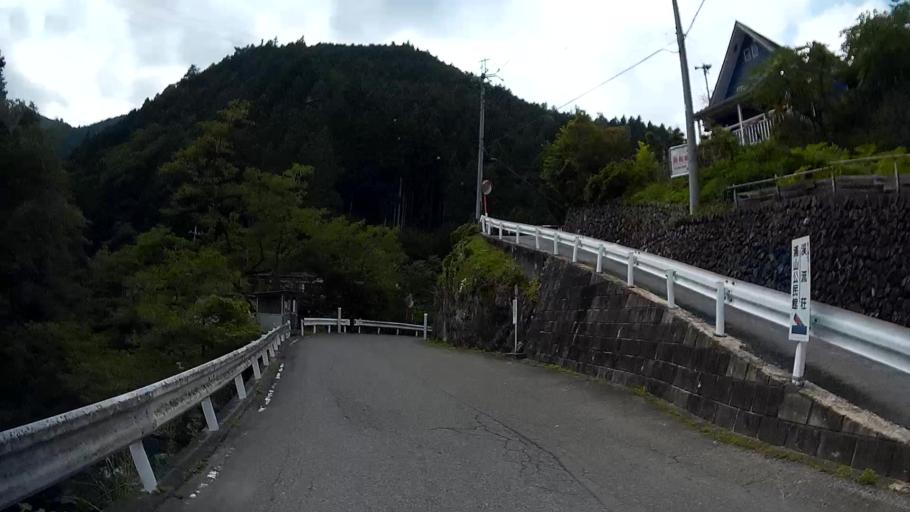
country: JP
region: Saitama
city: Chichibu
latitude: 35.9106
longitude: 139.0847
